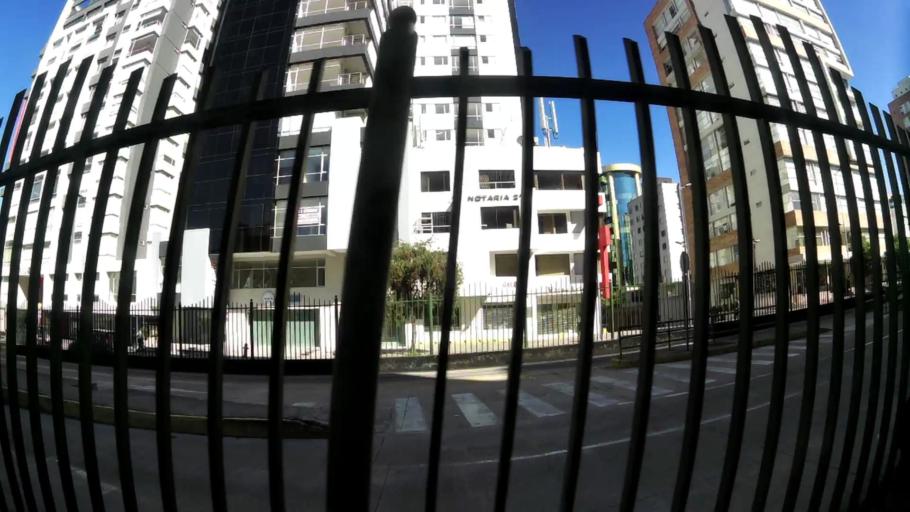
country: EC
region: Pichincha
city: Quito
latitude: -0.1815
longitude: -78.4786
